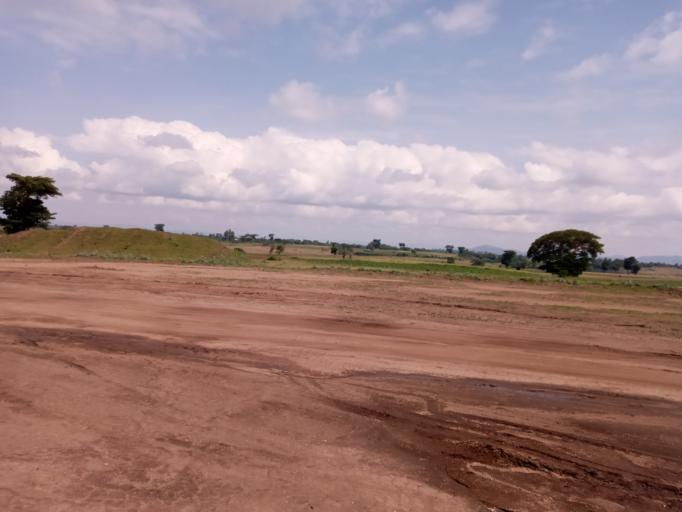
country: ET
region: Oromiya
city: Shashemene
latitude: 7.2868
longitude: 38.6095
